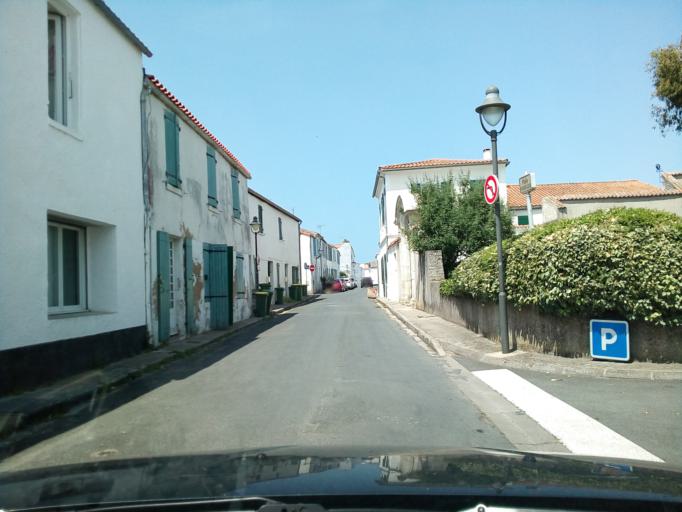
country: FR
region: Poitou-Charentes
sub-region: Departement de la Charente-Maritime
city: Dolus-d'Oleron
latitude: 45.9436
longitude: -1.3032
